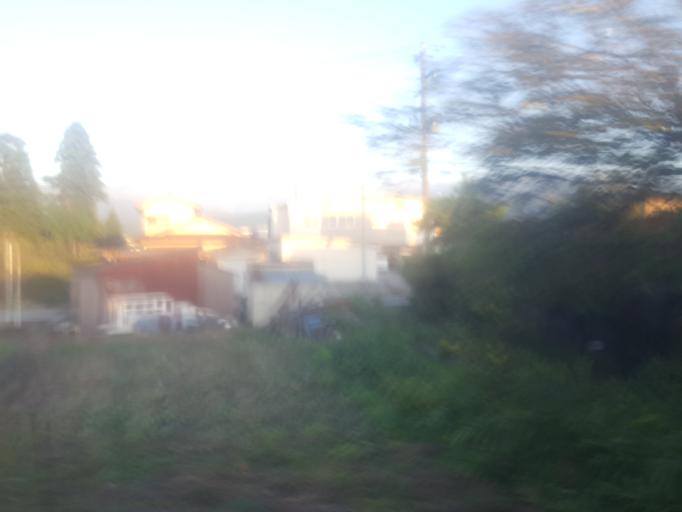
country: JP
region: Toyama
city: Kamiichi
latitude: 36.6712
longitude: 137.3163
